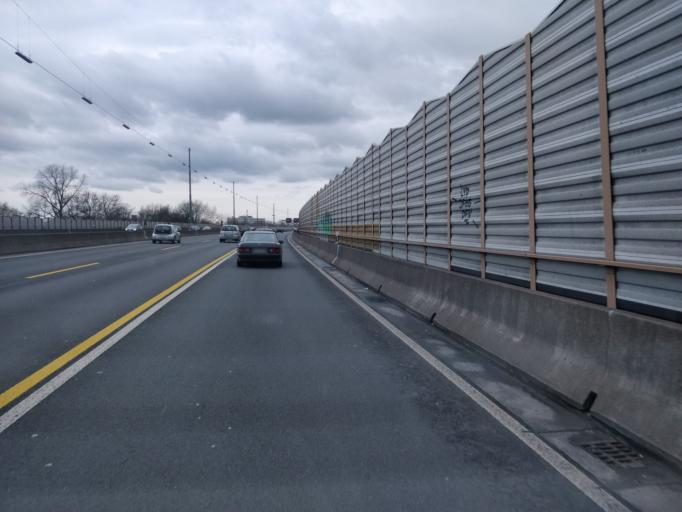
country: DE
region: North Rhine-Westphalia
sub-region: Regierungsbezirk Koln
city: Leverkusen
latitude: 51.0392
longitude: 6.9982
